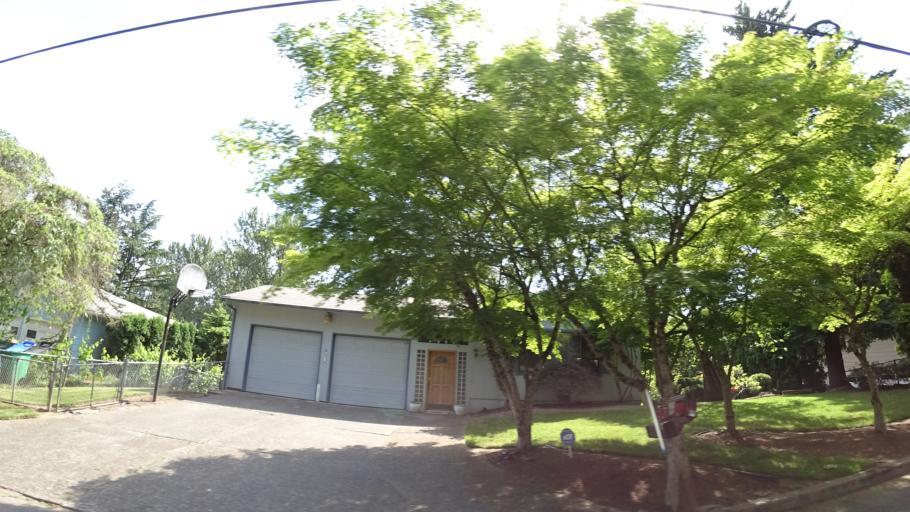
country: US
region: Oregon
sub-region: Washington County
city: Metzger
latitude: 45.4496
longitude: -122.7428
